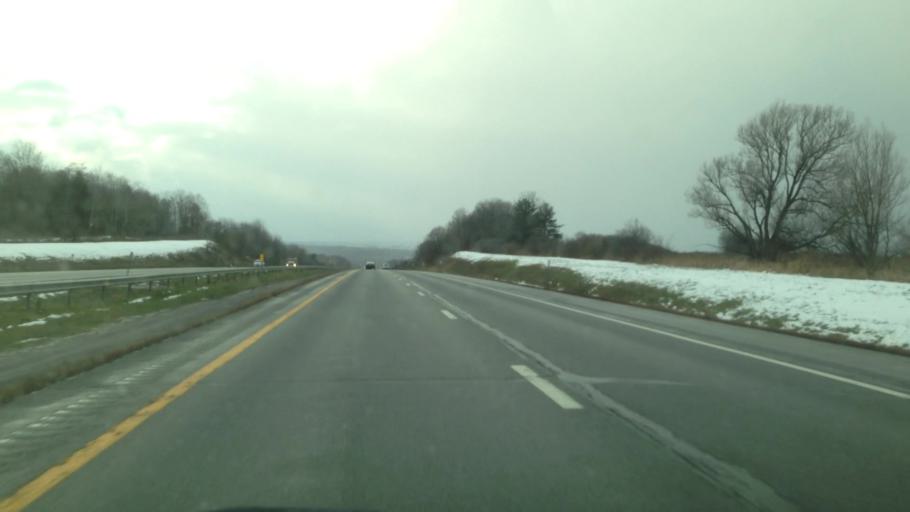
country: US
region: New York
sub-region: Montgomery County
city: Tribes Hill
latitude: 42.9331
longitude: -74.2549
